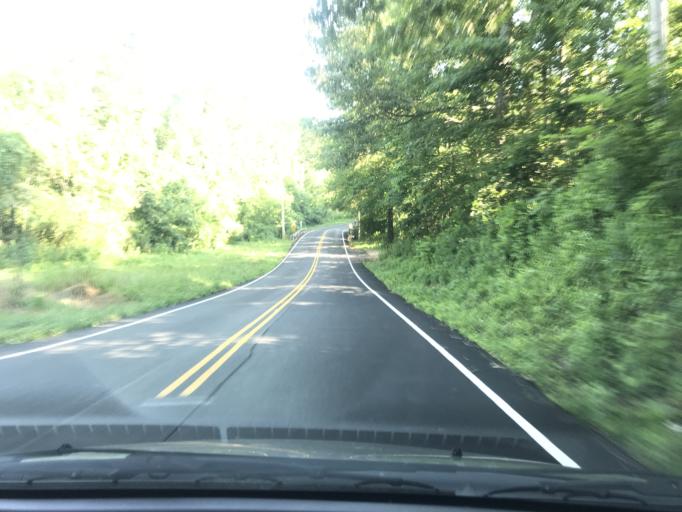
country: US
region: Tennessee
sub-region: Loudon County
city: Loudon
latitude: 35.7926
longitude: -84.3625
